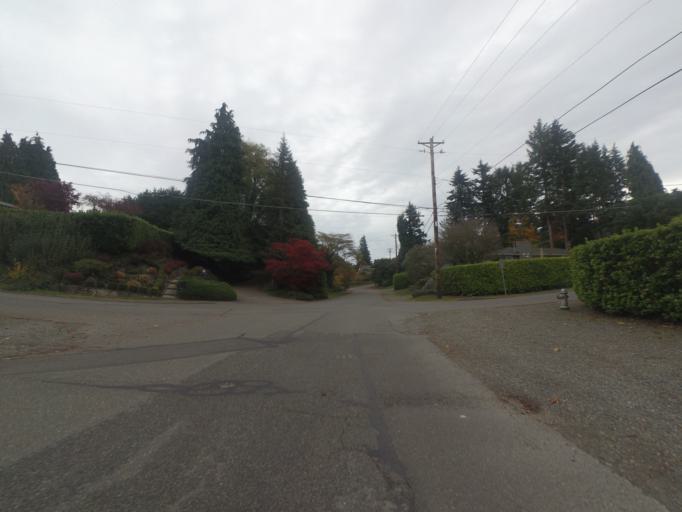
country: US
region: Washington
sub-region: Pierce County
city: University Place
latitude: 47.2210
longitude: -122.5644
